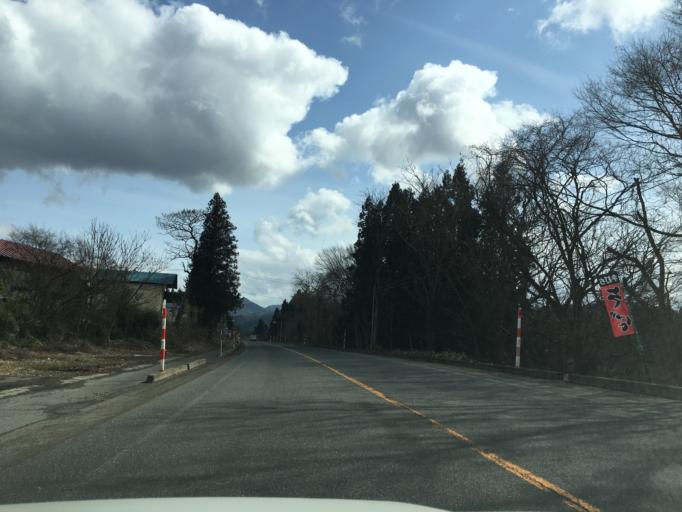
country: JP
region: Akita
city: Odate
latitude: 40.2250
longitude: 140.6020
